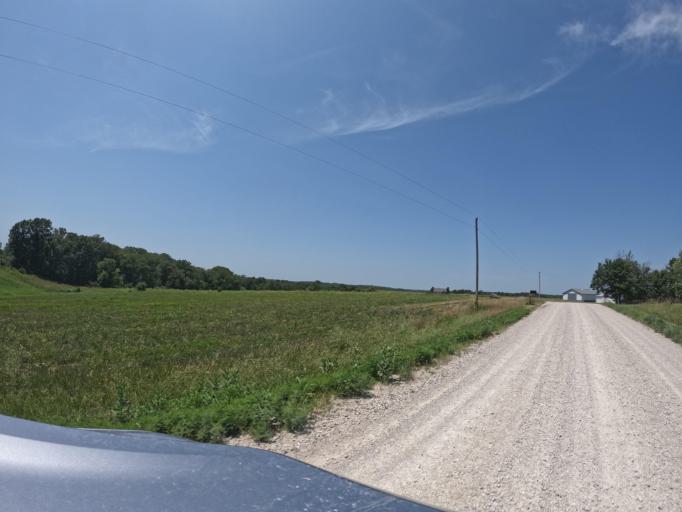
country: US
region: Iowa
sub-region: Henry County
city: Mount Pleasant
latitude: 40.9140
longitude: -91.6584
